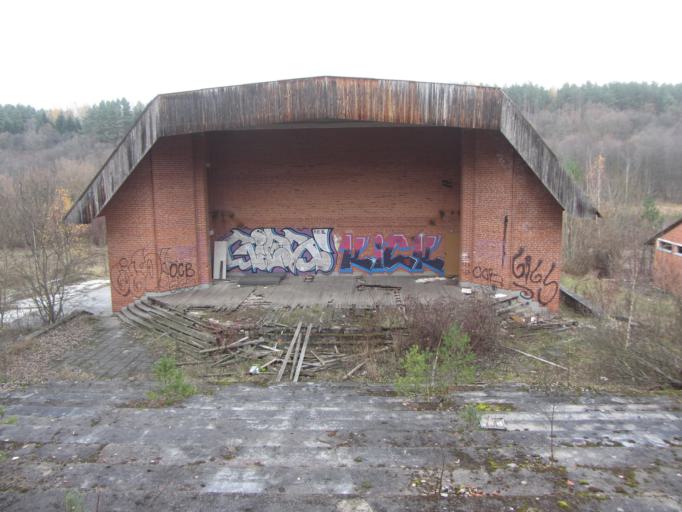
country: LT
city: Grigiskes
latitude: 54.7204
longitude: 25.0511
